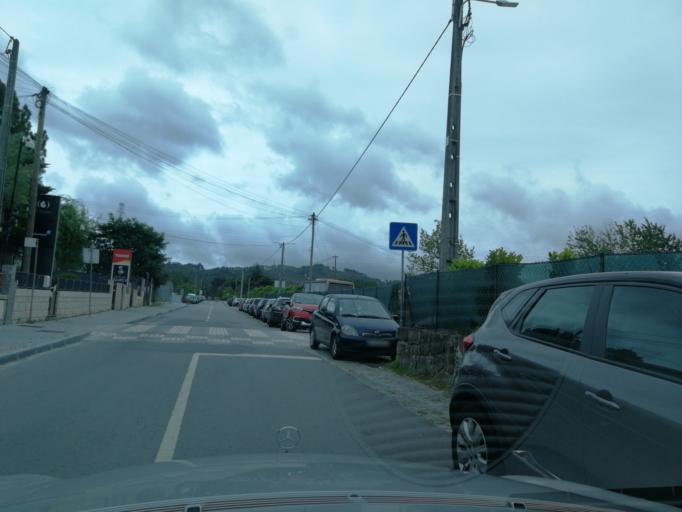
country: PT
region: Braga
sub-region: Braga
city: Adaufe
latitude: 41.6036
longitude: -8.3816
